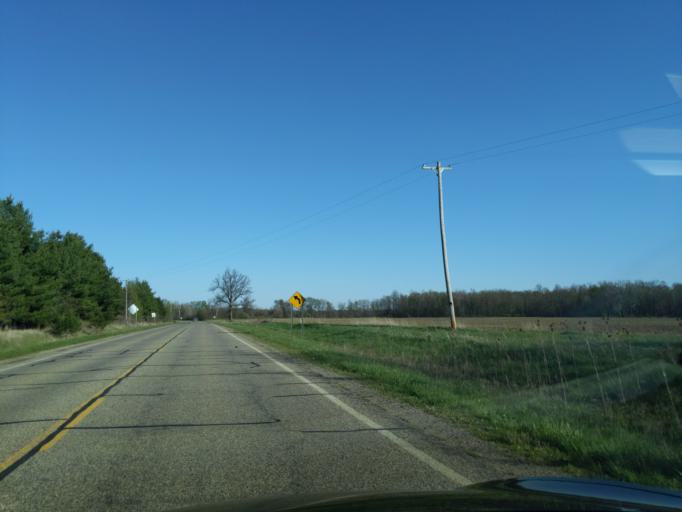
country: US
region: Michigan
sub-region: Ionia County
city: Portland
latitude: 42.8844
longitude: -84.9889
